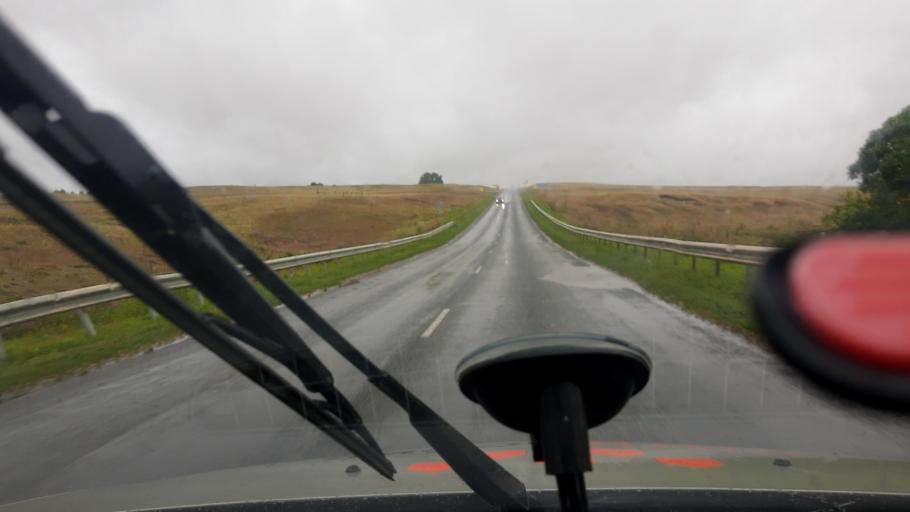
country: RU
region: Bashkortostan
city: Chekmagush
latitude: 55.0275
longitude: 54.6043
